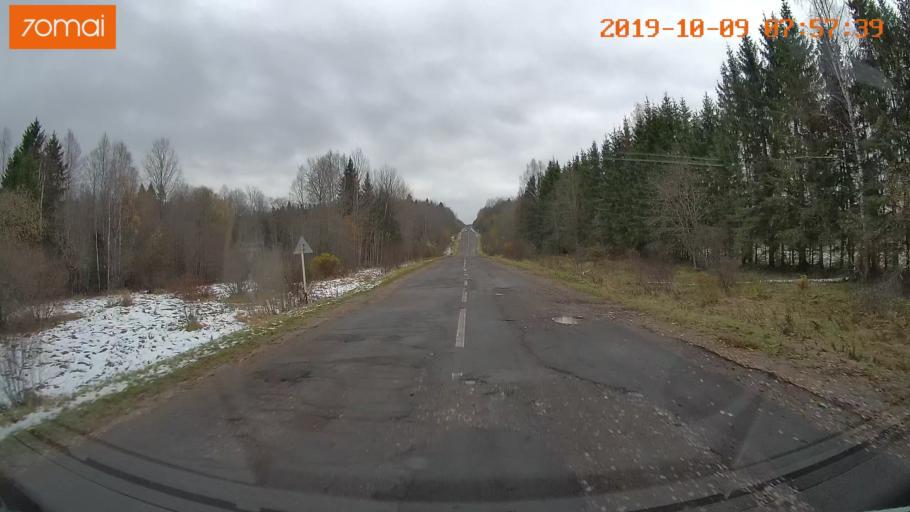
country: RU
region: Jaroslavl
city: Kukoboy
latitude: 58.6970
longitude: 39.9540
